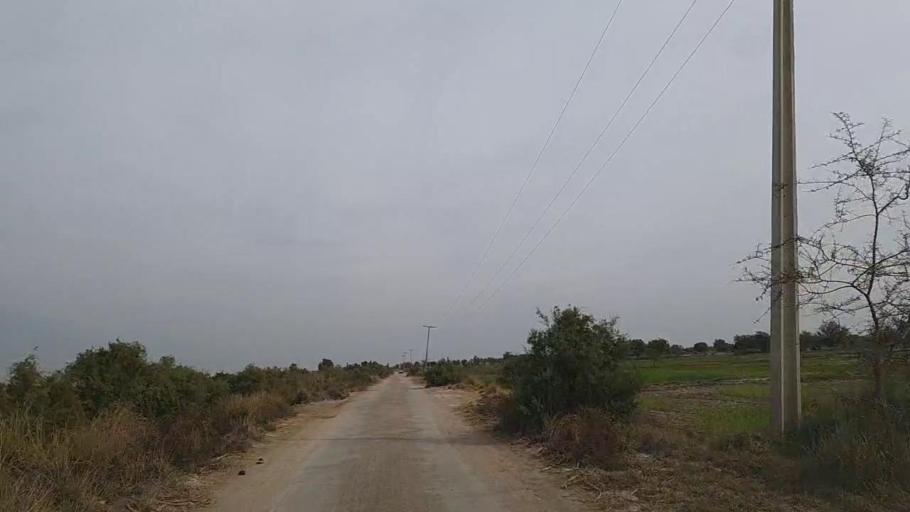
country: PK
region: Sindh
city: Jam Sahib
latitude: 26.4000
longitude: 68.5350
